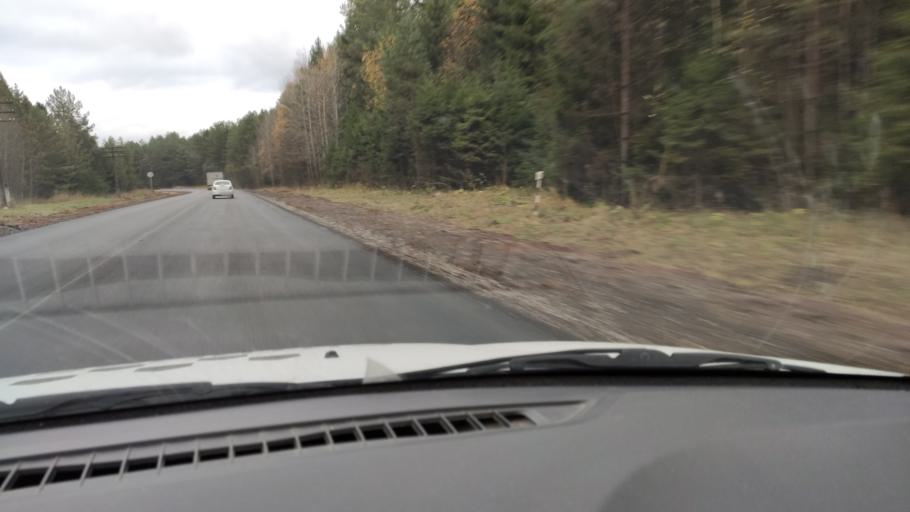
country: RU
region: Kirov
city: Slobodskoy
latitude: 58.7808
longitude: 50.4800
